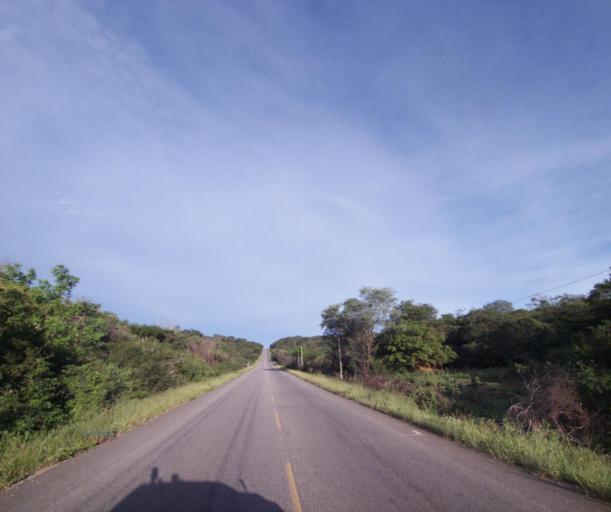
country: BR
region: Bahia
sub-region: Caetite
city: Caetite
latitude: -14.1719
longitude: -42.2172
